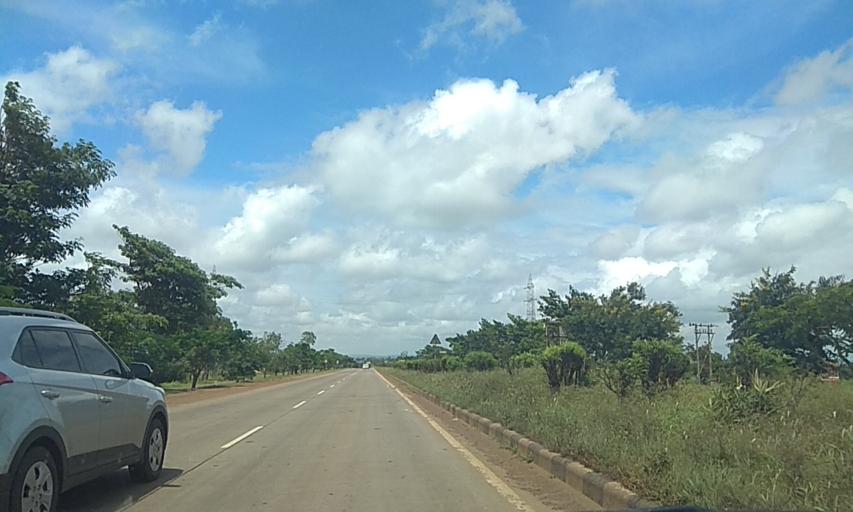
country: IN
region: Karnataka
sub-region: Belgaum
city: Sankeshwar
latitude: 16.1486
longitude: 74.5173
